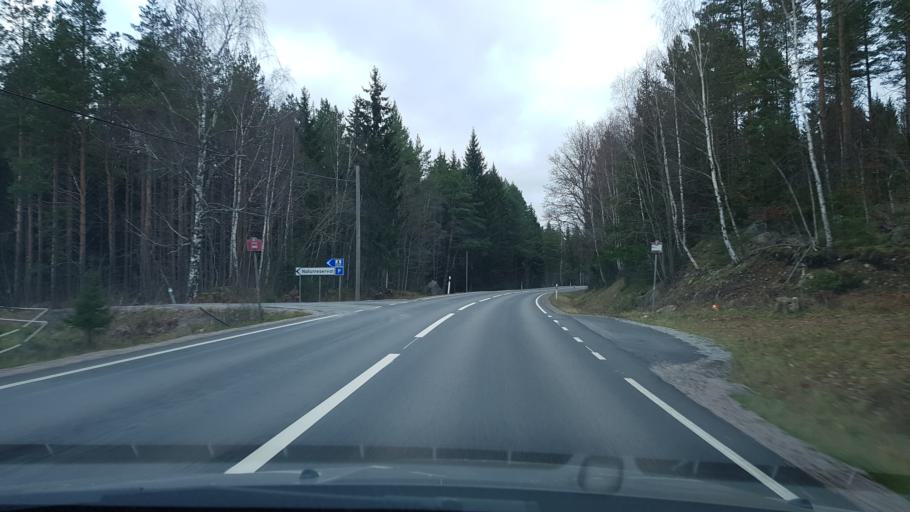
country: SE
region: Stockholm
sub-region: Norrtalje Kommun
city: Skanninge
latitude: 60.0102
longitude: 18.3339
